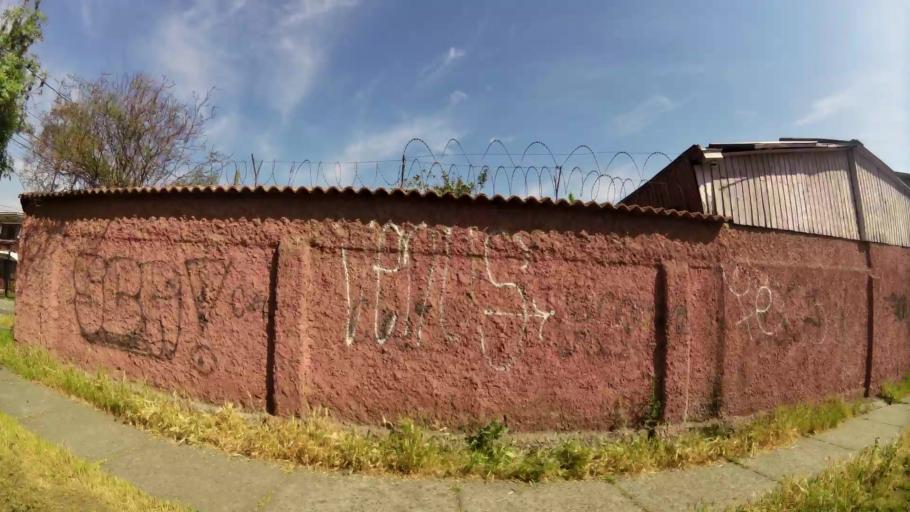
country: CL
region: Santiago Metropolitan
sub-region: Provincia de Maipo
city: San Bernardo
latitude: -33.5579
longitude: -70.6720
